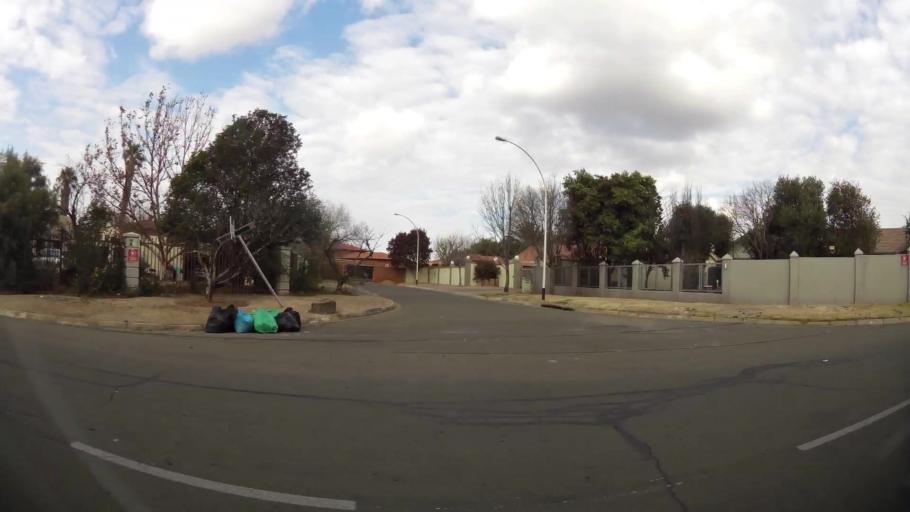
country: ZA
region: Orange Free State
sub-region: Mangaung Metropolitan Municipality
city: Bloemfontein
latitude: -29.0770
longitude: 26.2112
